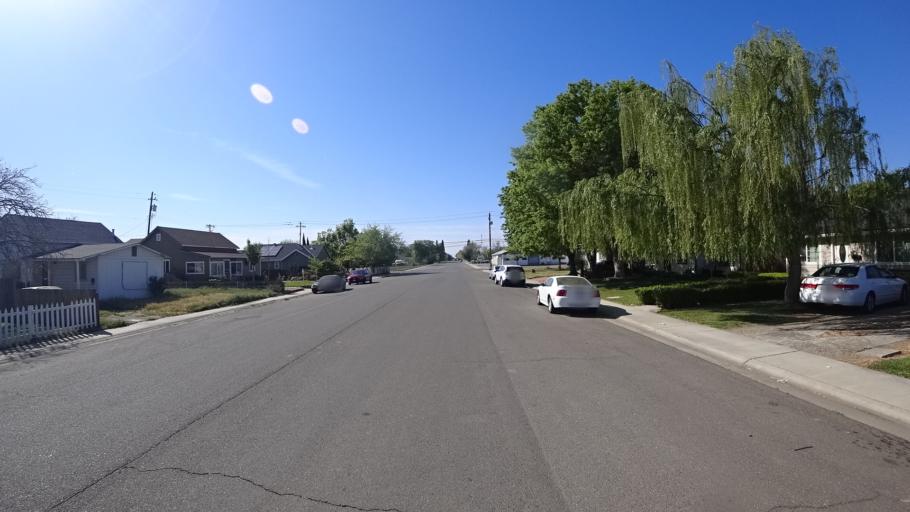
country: US
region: California
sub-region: Glenn County
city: Willows
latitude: 39.5275
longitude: -122.1954
